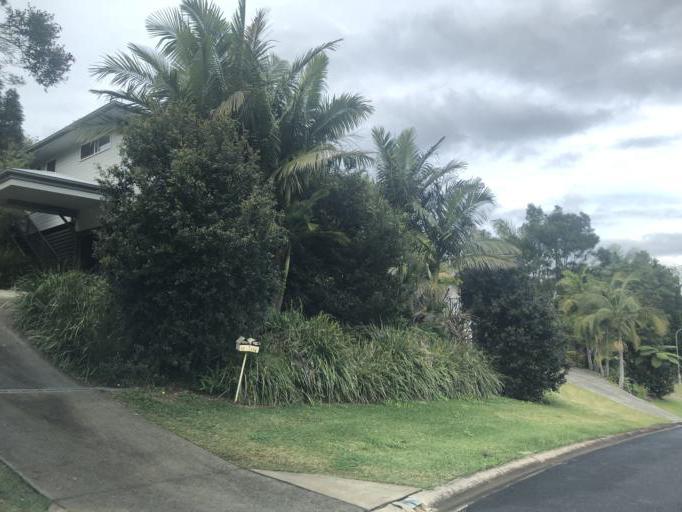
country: AU
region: New South Wales
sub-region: Coffs Harbour
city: Coffs Harbour
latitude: -30.2766
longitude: 153.1094
